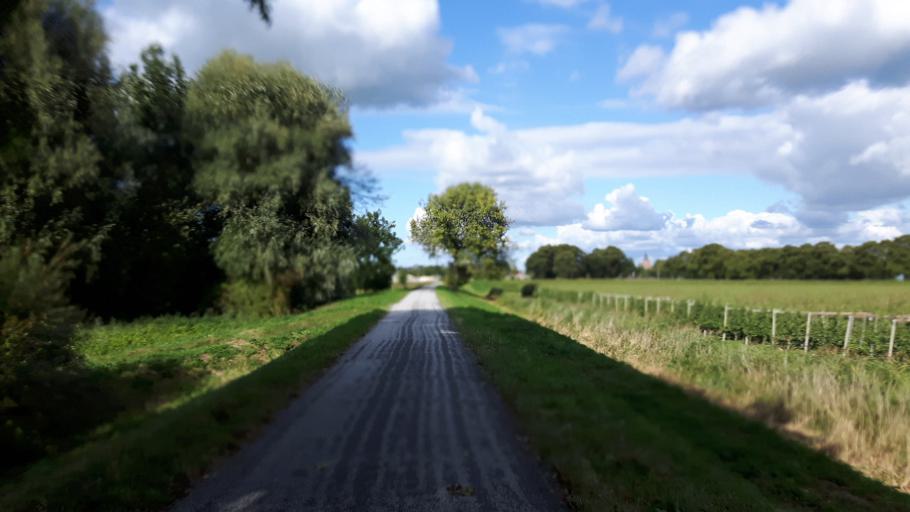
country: NL
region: South Holland
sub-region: Gemeente Leerdam
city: Leerdam
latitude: 51.8835
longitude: 5.0889
